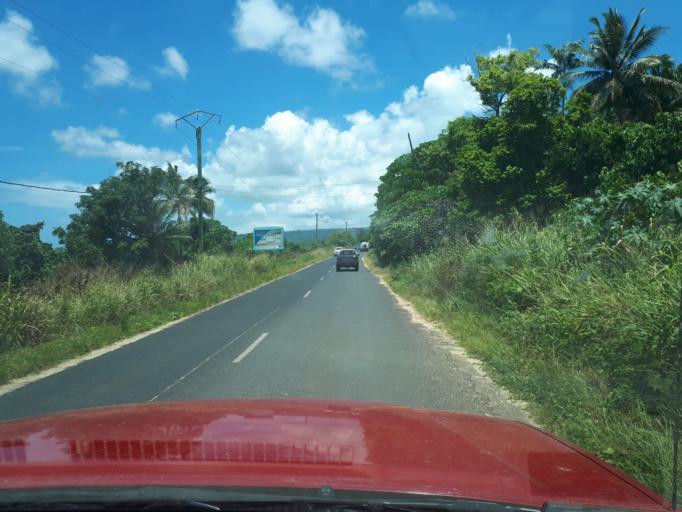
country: VU
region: Sanma
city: Luganville
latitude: -15.5154
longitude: 167.2049
